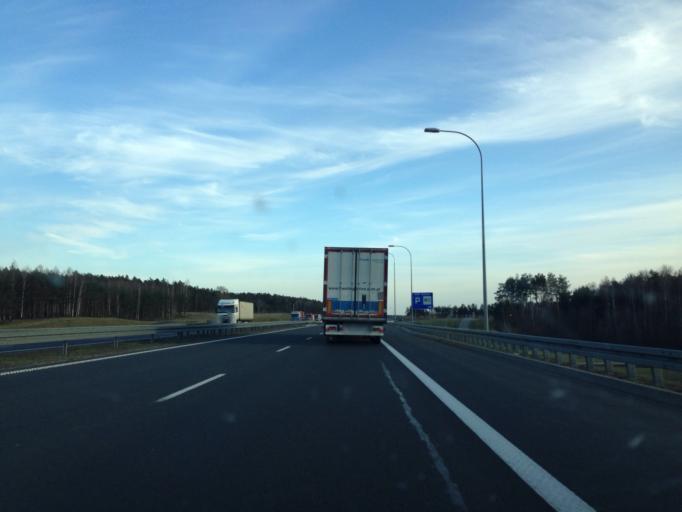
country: PL
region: Kujawsko-Pomorskie
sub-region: Powiat swiecki
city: Warlubie
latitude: 53.6491
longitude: 18.6404
